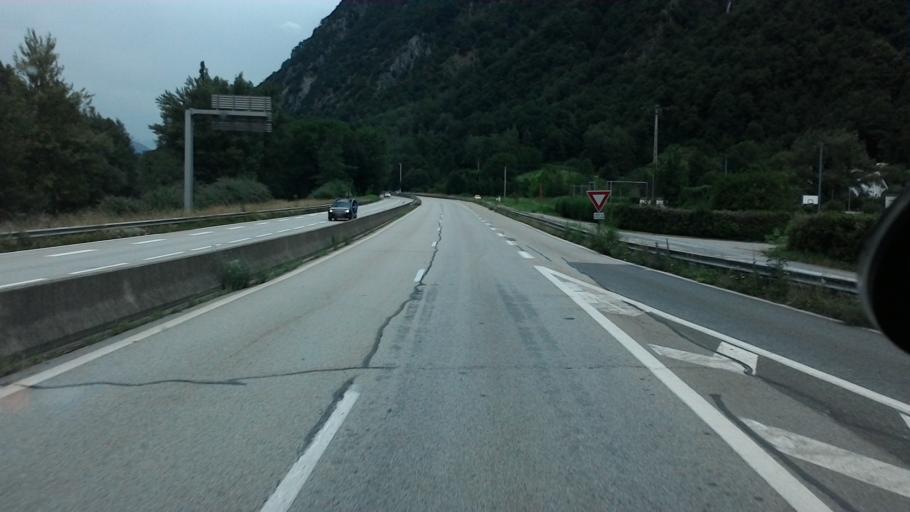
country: FR
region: Rhone-Alpes
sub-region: Departement de la Savoie
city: La Bathie
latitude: 45.5635
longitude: 6.4691
